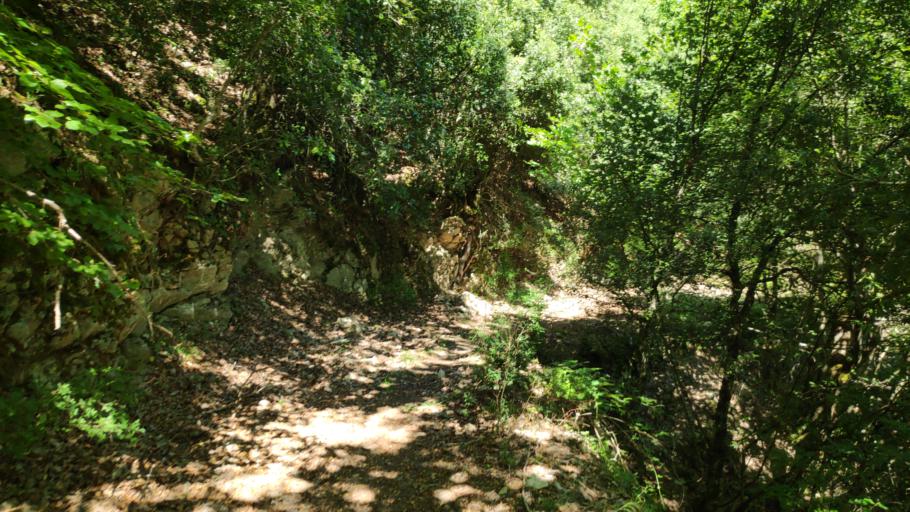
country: IT
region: Calabria
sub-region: Provincia di Vibo-Valentia
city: Nardodipace
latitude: 38.4826
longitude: 16.3817
